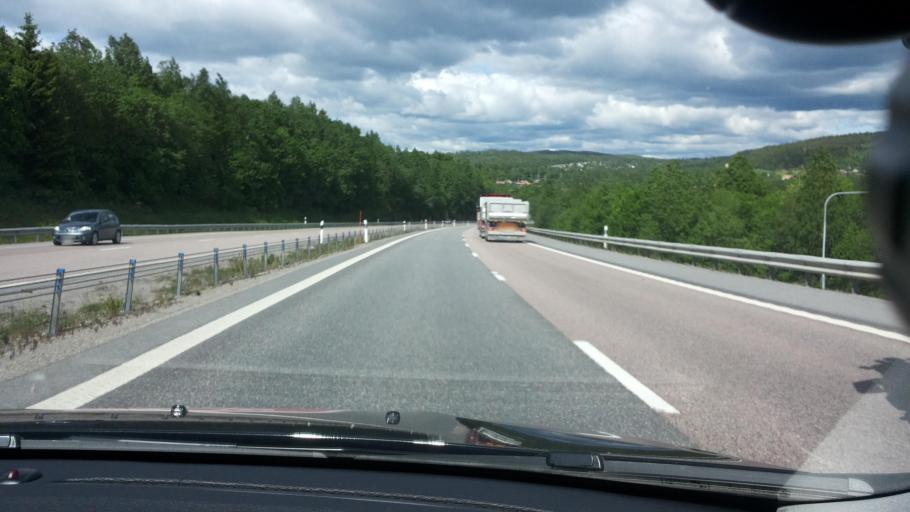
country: SE
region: Vaesternorrland
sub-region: Timra Kommun
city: Timra
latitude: 62.4678
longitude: 17.3225
